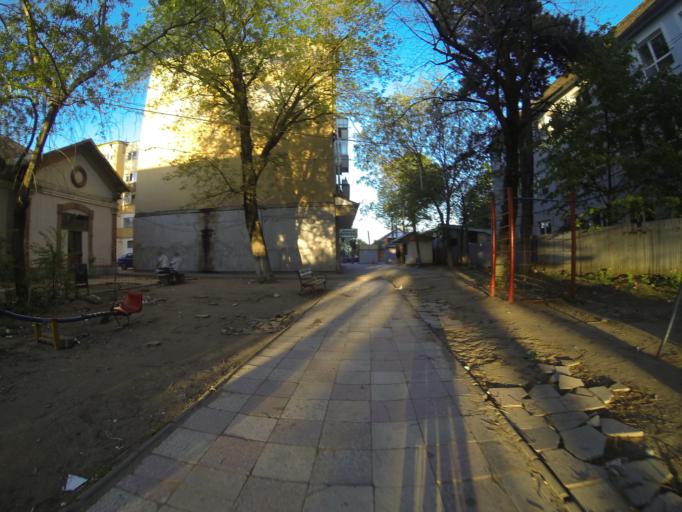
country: RO
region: Dolj
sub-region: Comuna Segarcea
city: Segarcea
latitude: 44.0999
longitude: 23.7432
